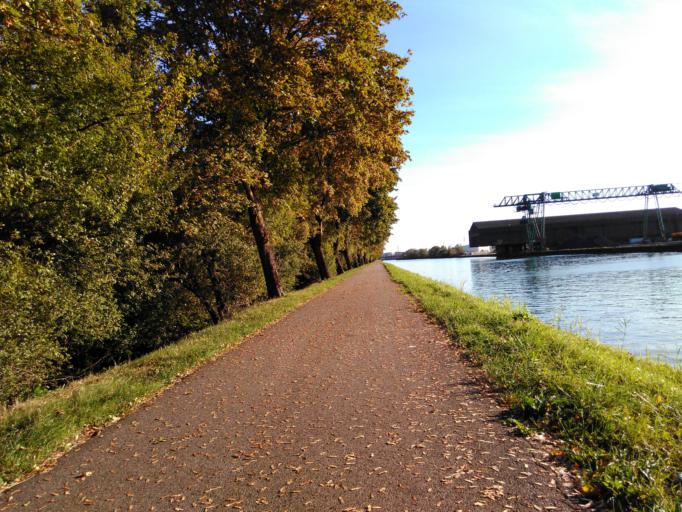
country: FR
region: Lorraine
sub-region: Departement de la Moselle
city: Mondelange
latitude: 49.2718
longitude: 6.1818
